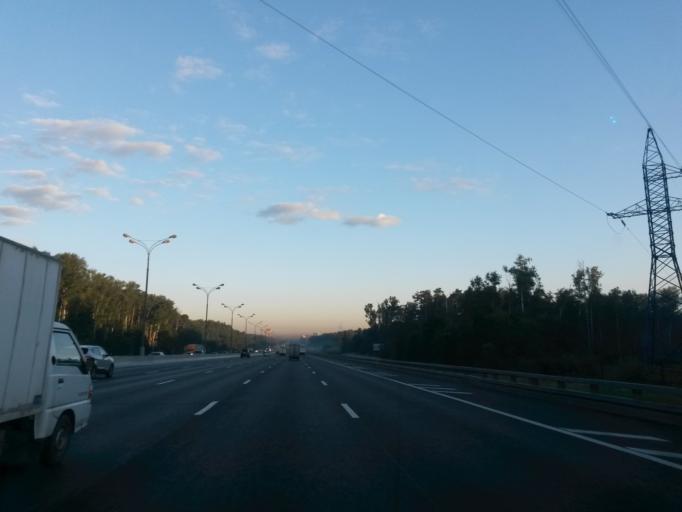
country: RU
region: Moskovskaya
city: Druzhba
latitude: 55.8607
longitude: 37.7686
